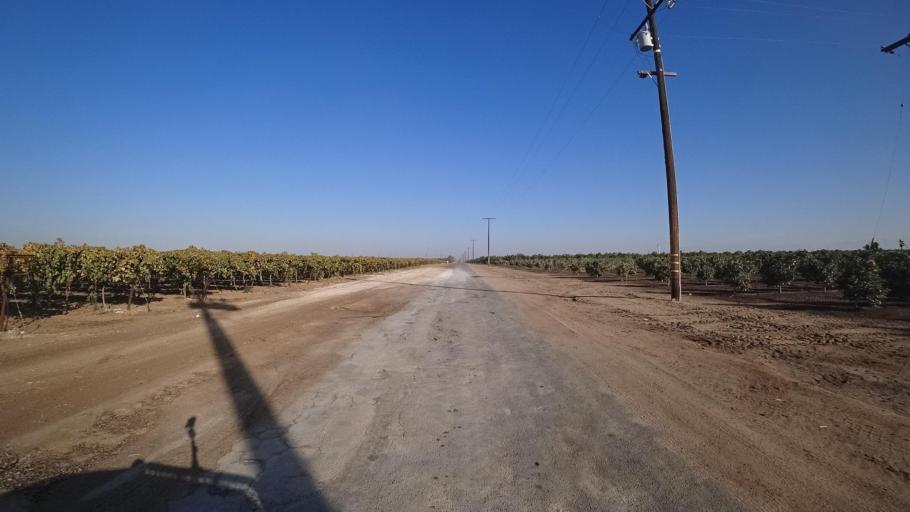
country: US
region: California
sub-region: Tulare County
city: Richgrove
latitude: 35.7695
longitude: -119.1608
